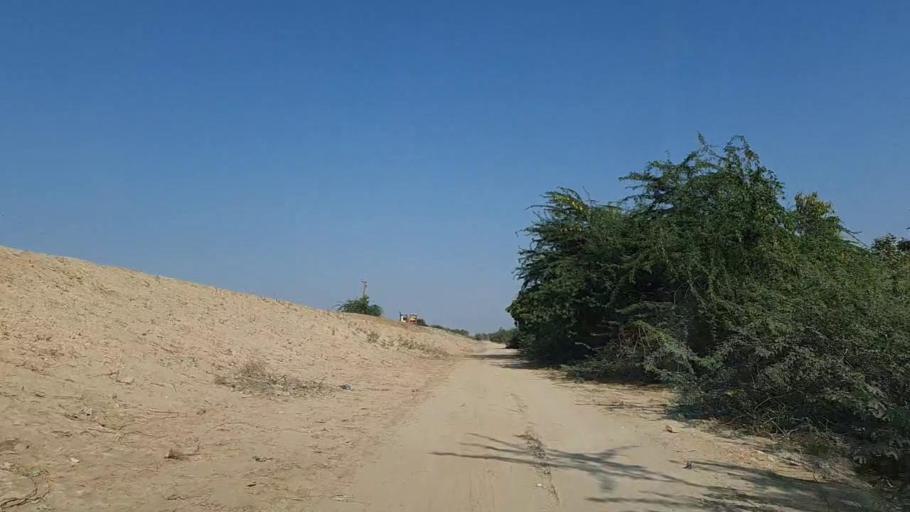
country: PK
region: Sindh
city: Thatta
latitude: 24.5833
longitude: 68.0320
